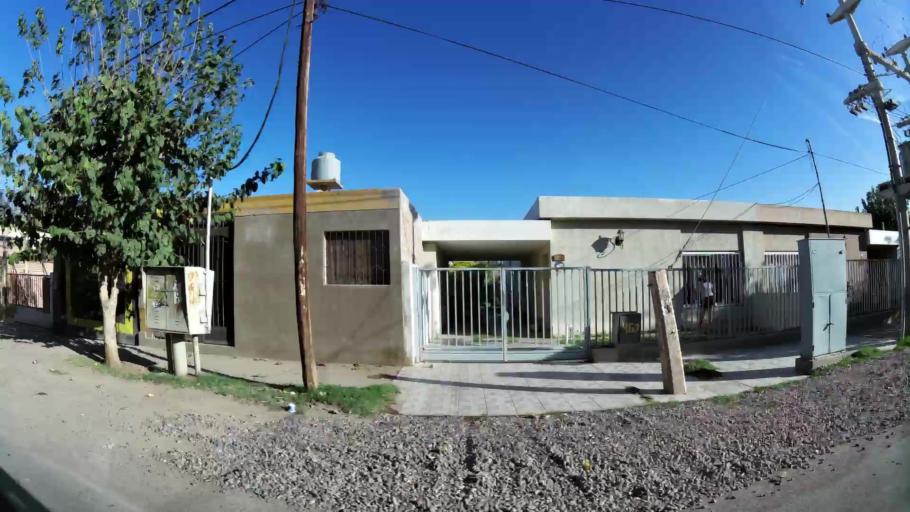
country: AR
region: San Juan
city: Villa Krause
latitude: -31.5587
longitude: -68.5156
